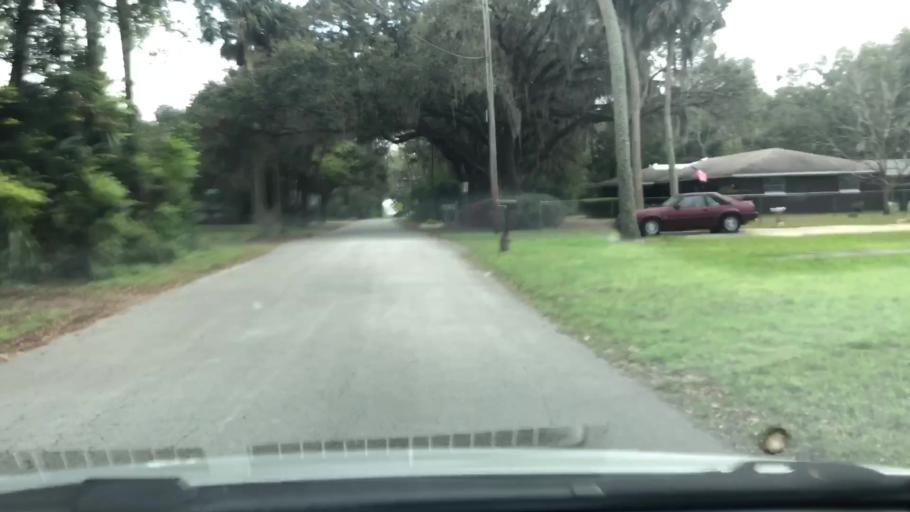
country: US
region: Florida
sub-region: Volusia County
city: Deltona
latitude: 28.8712
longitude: -81.2676
